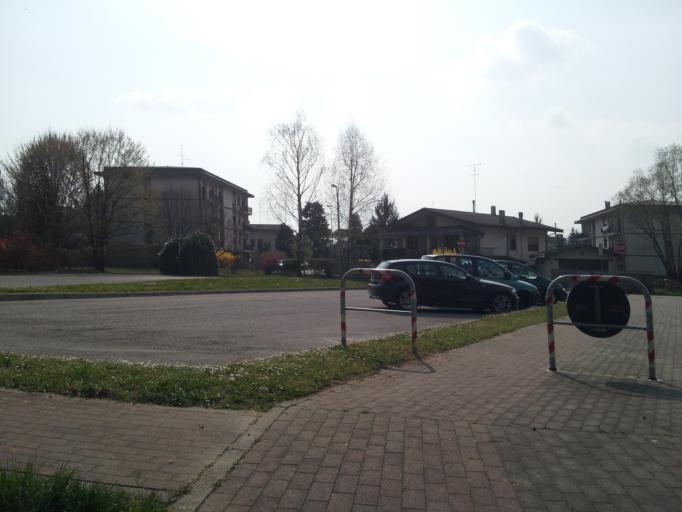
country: IT
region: Friuli Venezia Giulia
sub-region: Provincia di Pordenone
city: Pasiano
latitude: 45.8498
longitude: 12.6245
